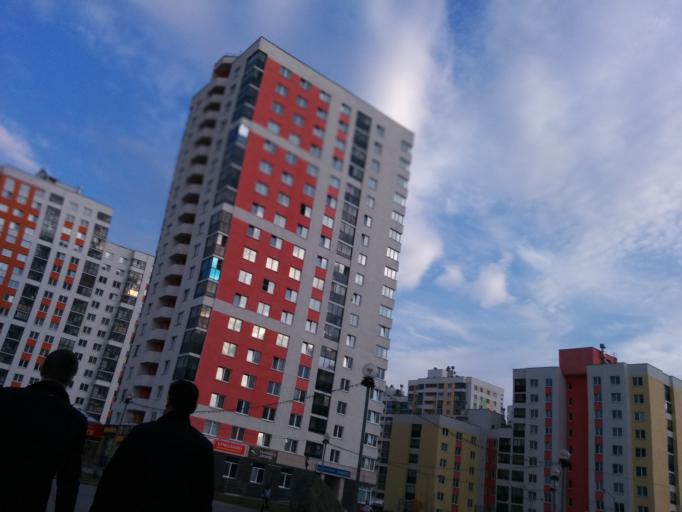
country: RU
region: Sverdlovsk
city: Sovkhoznyy
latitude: 56.7907
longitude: 60.5255
